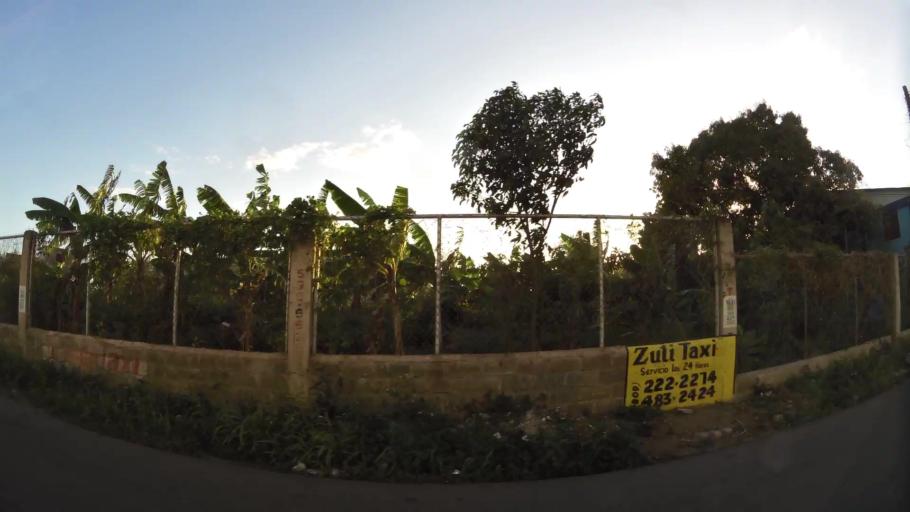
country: DO
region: Santo Domingo
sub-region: Santo Domingo
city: Santo Domingo Este
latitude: 18.4938
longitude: -69.8136
